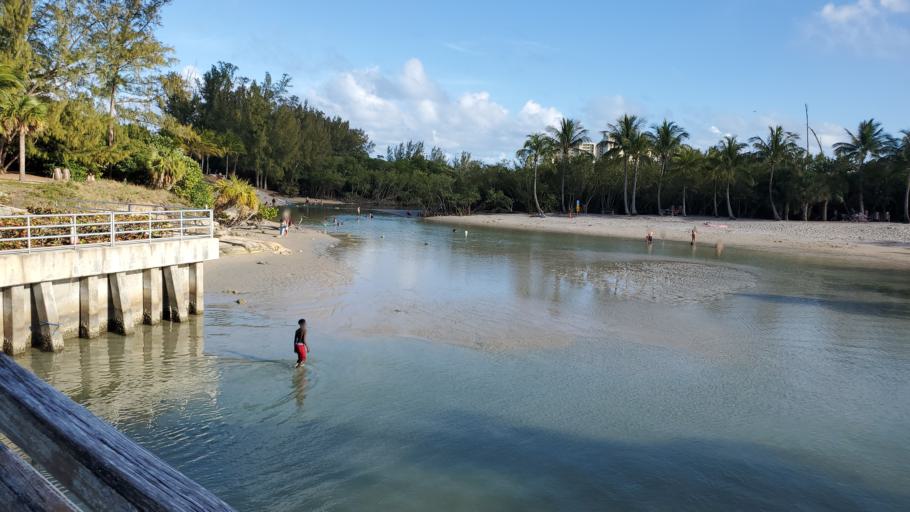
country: US
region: Florida
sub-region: Palm Beach County
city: Jupiter
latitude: 26.9436
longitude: -80.0745
